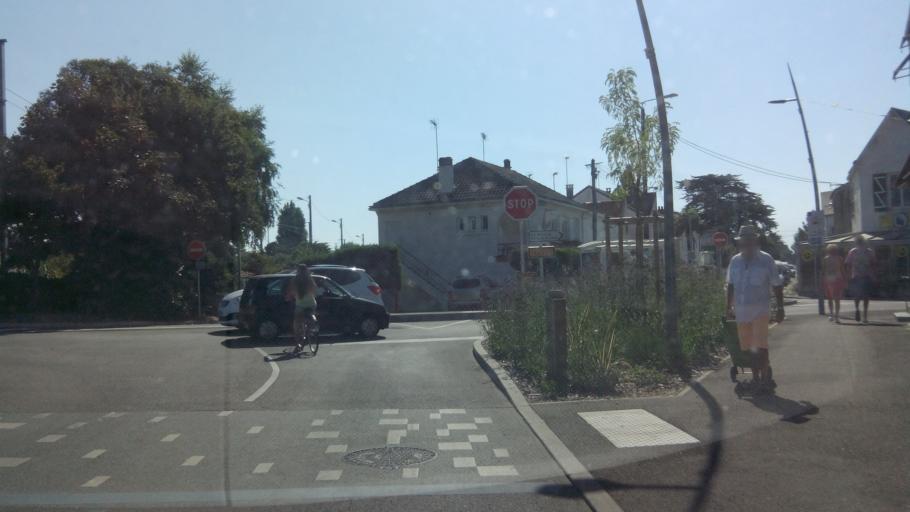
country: FR
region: Pays de la Loire
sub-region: Departement de la Loire-Atlantique
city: Pornichet
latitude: 47.2699
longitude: -2.3436
